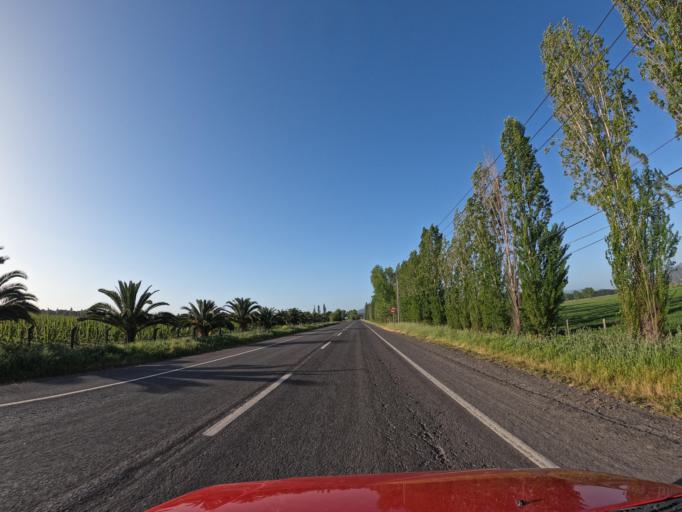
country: CL
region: O'Higgins
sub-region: Provincia de Colchagua
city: Santa Cruz
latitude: -34.4822
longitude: -71.3602
